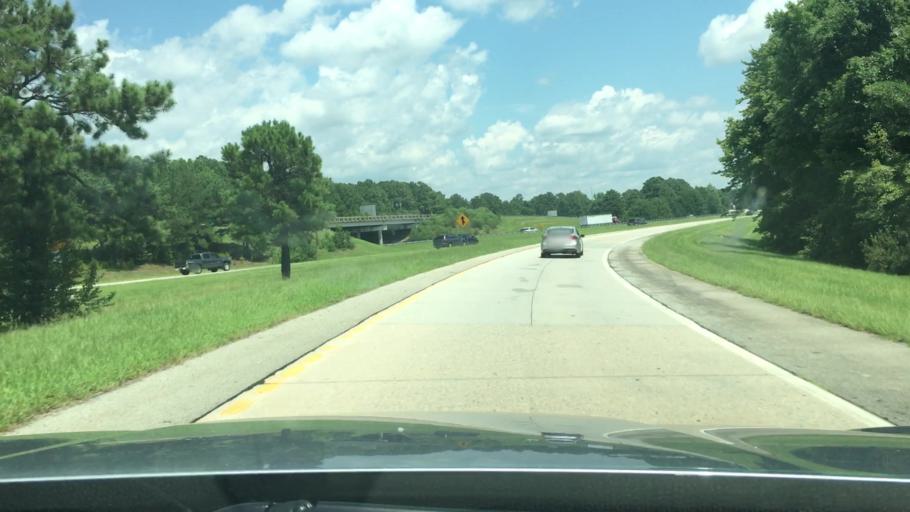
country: US
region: South Carolina
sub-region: Florence County
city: Florence
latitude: 34.1943
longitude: -79.8411
